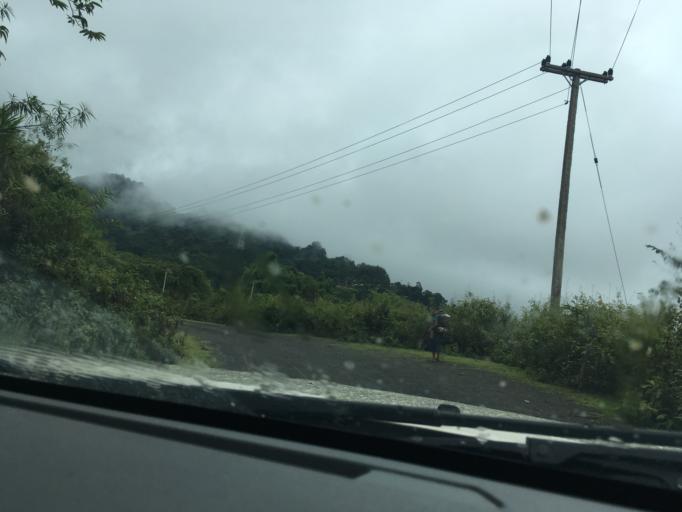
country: LA
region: Phongsali
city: Phongsali
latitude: 21.3560
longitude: 102.1153
